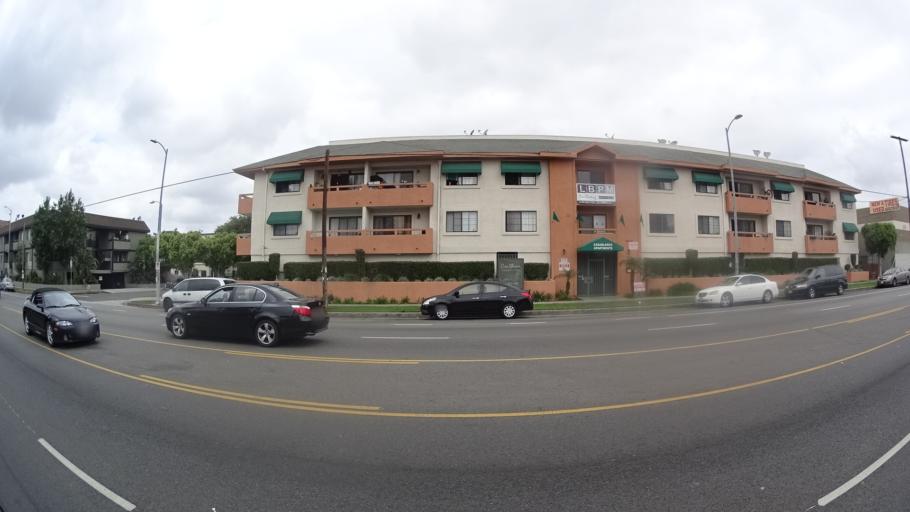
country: US
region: California
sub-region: Los Angeles County
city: San Fernando
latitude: 34.2416
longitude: -118.4502
